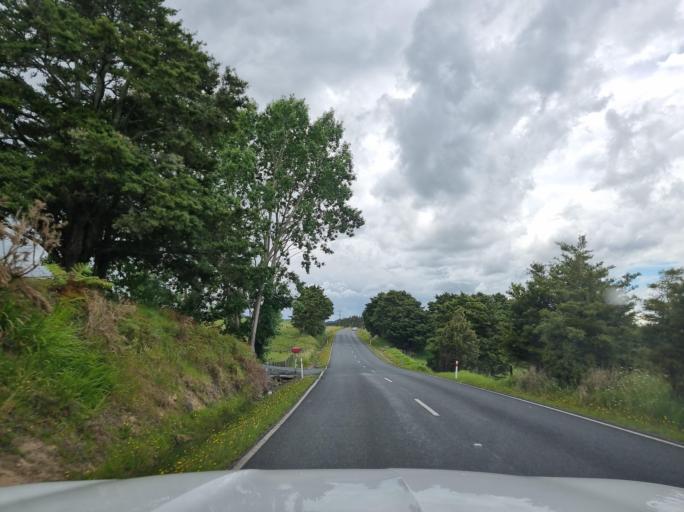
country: NZ
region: Northland
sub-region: Whangarei
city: Maungatapere
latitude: -35.8692
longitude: 174.2497
